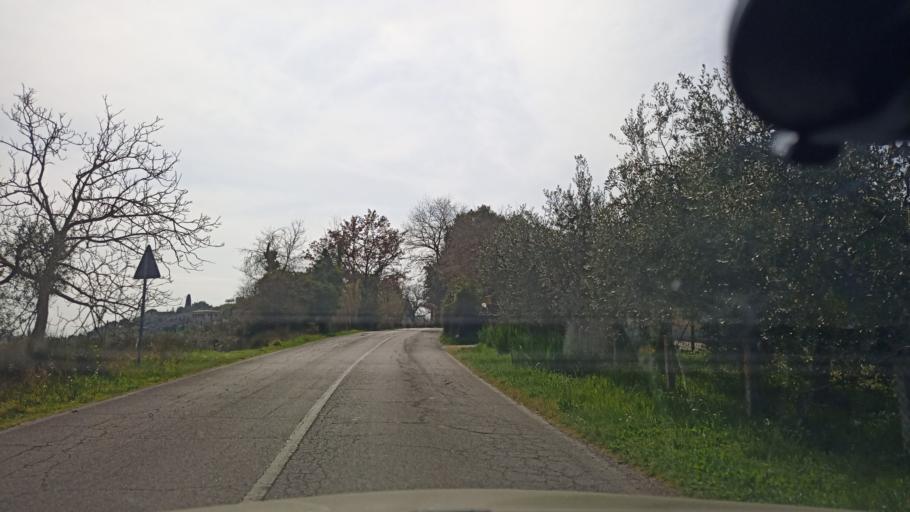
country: IT
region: Latium
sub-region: Provincia di Rieti
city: Torri in Sabina
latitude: 42.3590
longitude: 12.6517
